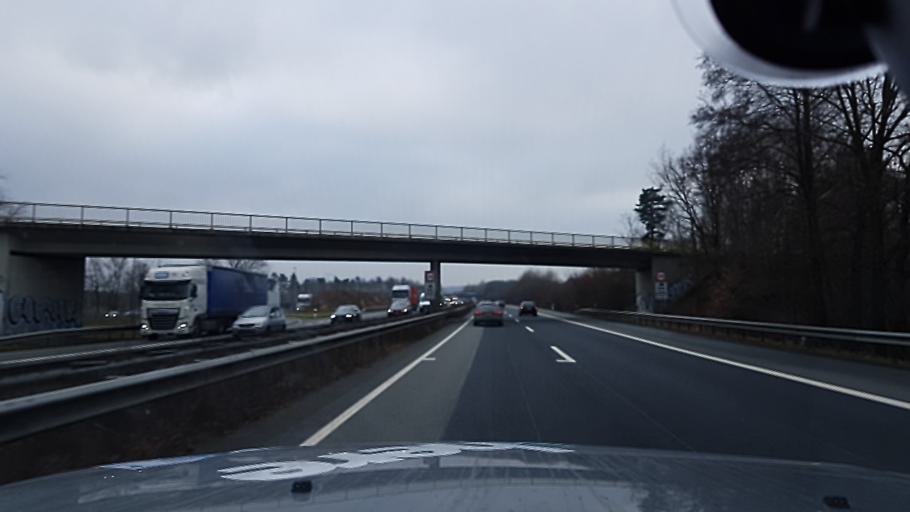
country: DE
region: Lower Saxony
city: Bramsche
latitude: 52.4170
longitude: 8.0309
